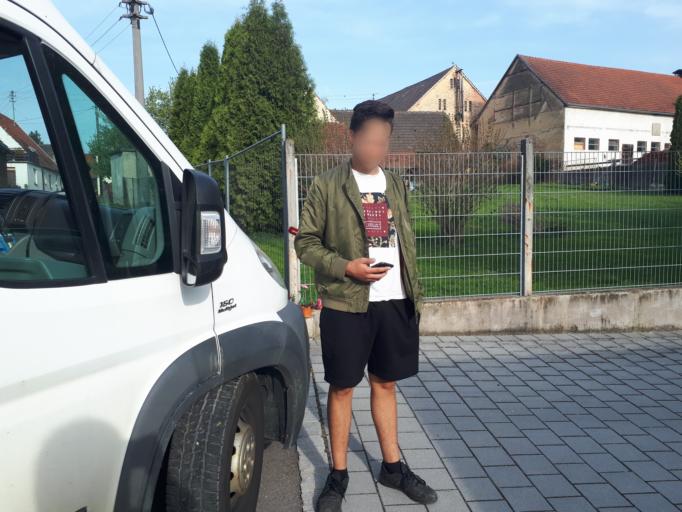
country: DE
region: Bavaria
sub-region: Swabia
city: Wertingen
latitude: 48.5641
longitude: 10.6847
